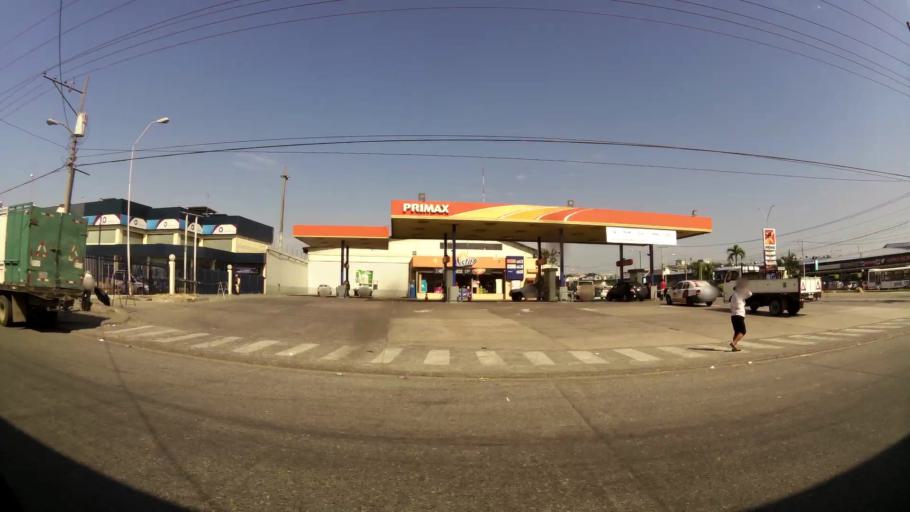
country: EC
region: Guayas
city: Santa Lucia
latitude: -2.0998
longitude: -79.9356
